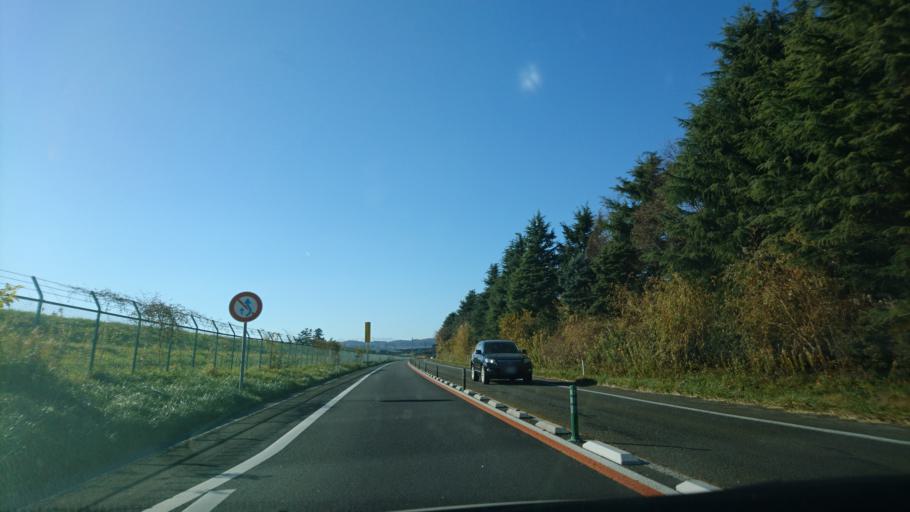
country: JP
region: Miyagi
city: Sendai
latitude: 38.2089
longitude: 140.8904
